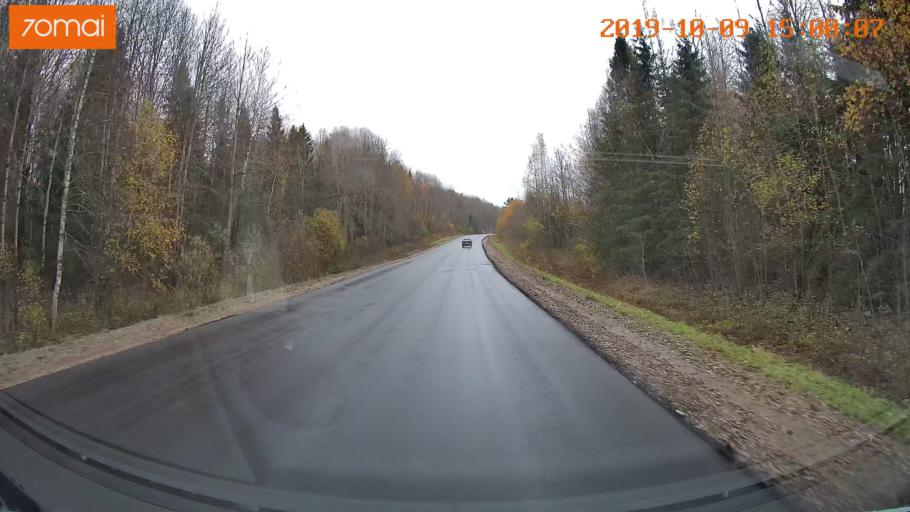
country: RU
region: Kostroma
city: Chistyye Bory
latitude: 58.3127
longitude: 41.6757
